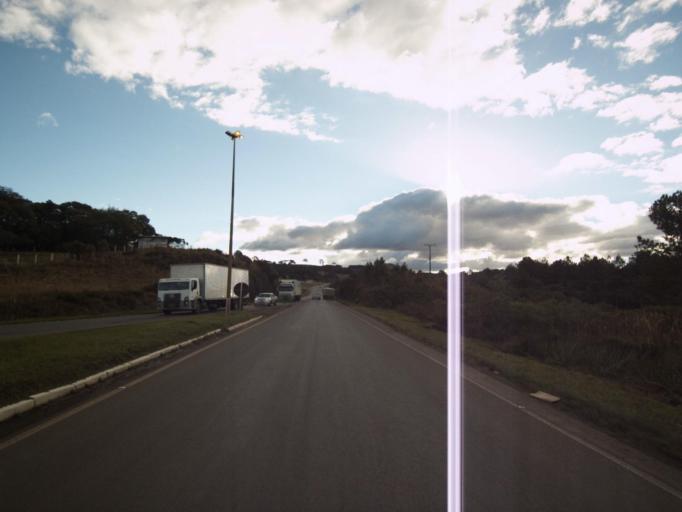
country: BR
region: Santa Catarina
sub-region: Campos Novos
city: Campos Novos
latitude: -27.3933
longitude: -51.1929
